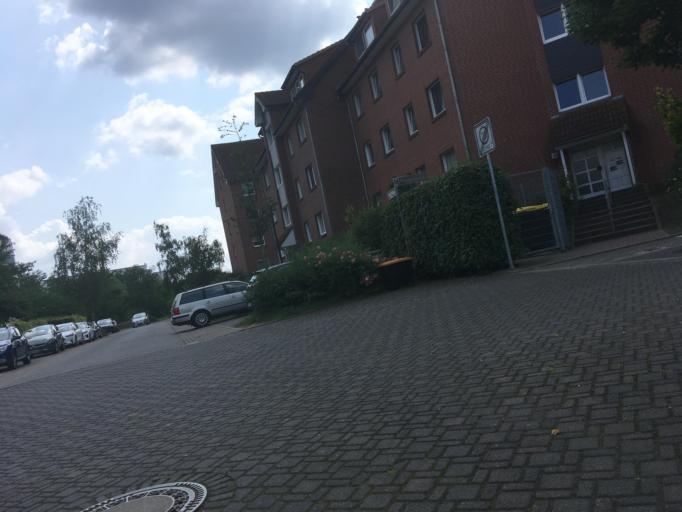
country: DE
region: Brandenburg
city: Wildau
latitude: 52.3272
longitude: 13.6200
